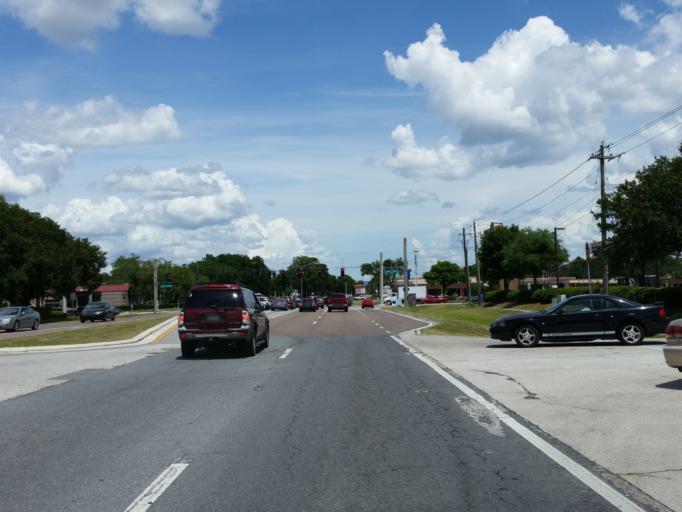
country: US
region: Florida
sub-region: Hillsborough County
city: Plant City
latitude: 27.9890
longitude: -82.1230
